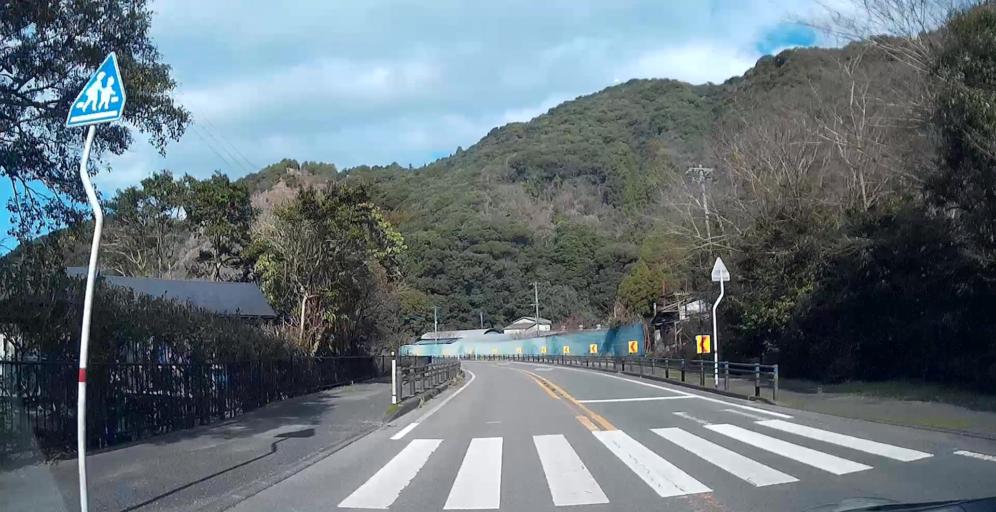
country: JP
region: Kumamoto
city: Yatsushiro
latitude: 32.4109
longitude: 130.5542
